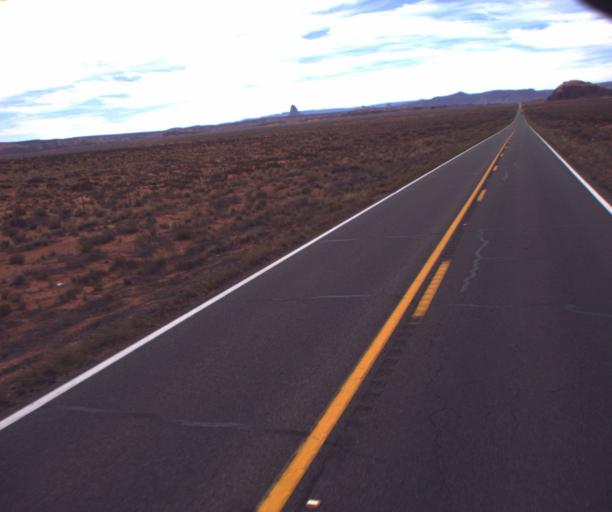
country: US
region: Arizona
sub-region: Navajo County
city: Kayenta
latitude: 36.9736
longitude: -110.1889
